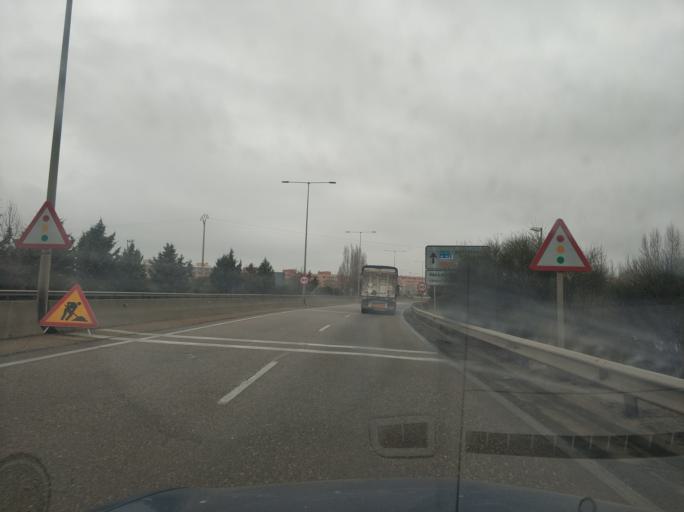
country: ES
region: Castille and Leon
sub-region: Provincia de Valladolid
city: Valladolid
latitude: 41.6392
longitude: -4.7027
